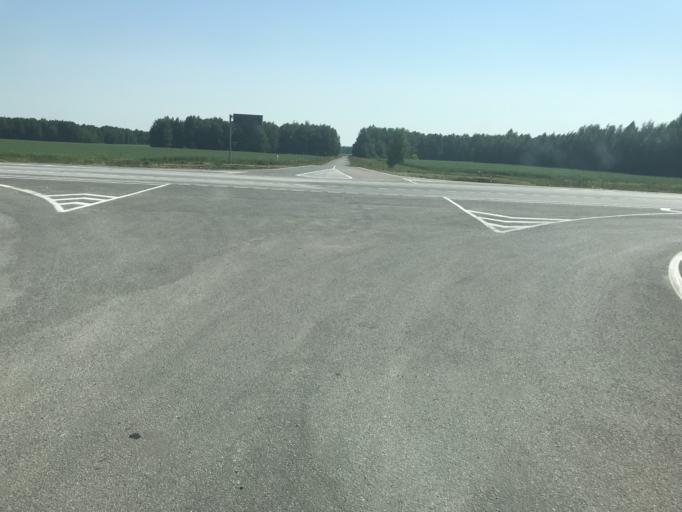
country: KZ
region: Soltustik Qazaqstan
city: Bishkul
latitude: 54.6638
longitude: 69.1474
